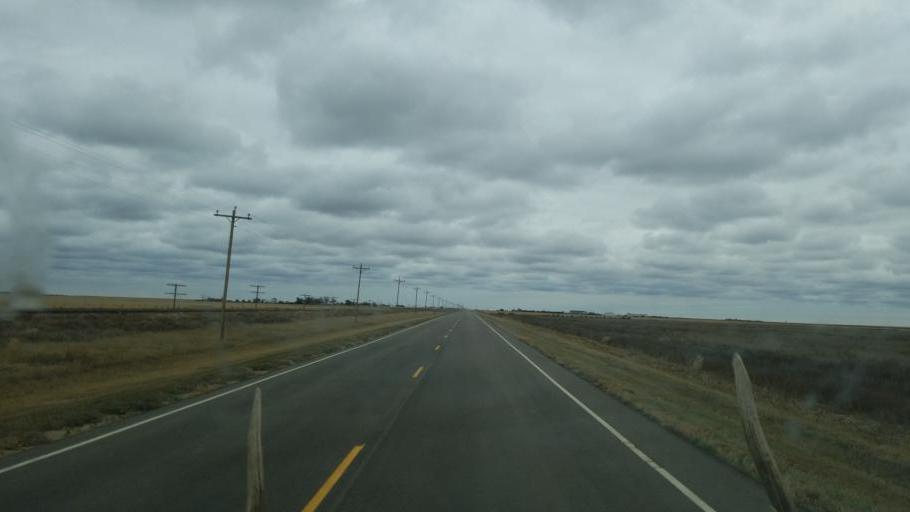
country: US
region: Colorado
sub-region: Kiowa County
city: Eads
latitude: 38.4859
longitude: -102.8552
